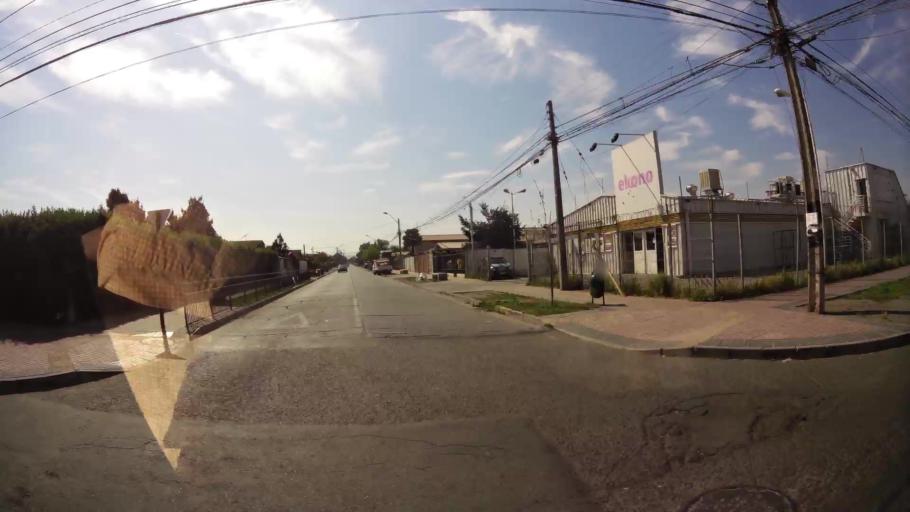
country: CL
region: Santiago Metropolitan
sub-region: Provincia de Talagante
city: Talagante
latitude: -33.6747
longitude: -70.9461
